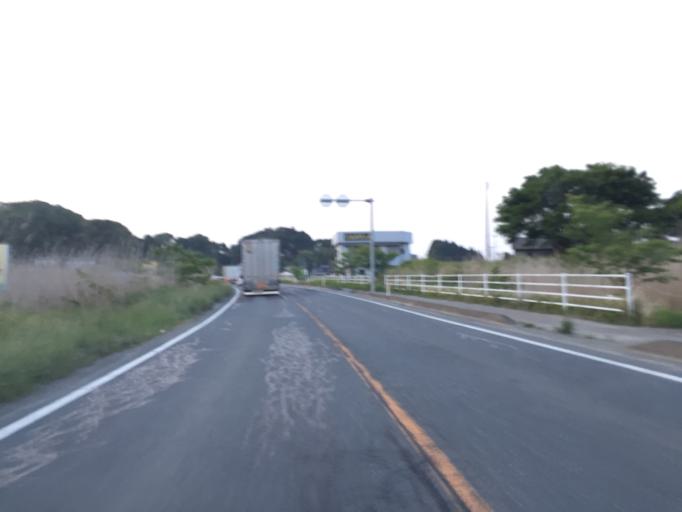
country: JP
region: Fukushima
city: Namie
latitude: 37.6069
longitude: 141.0070
